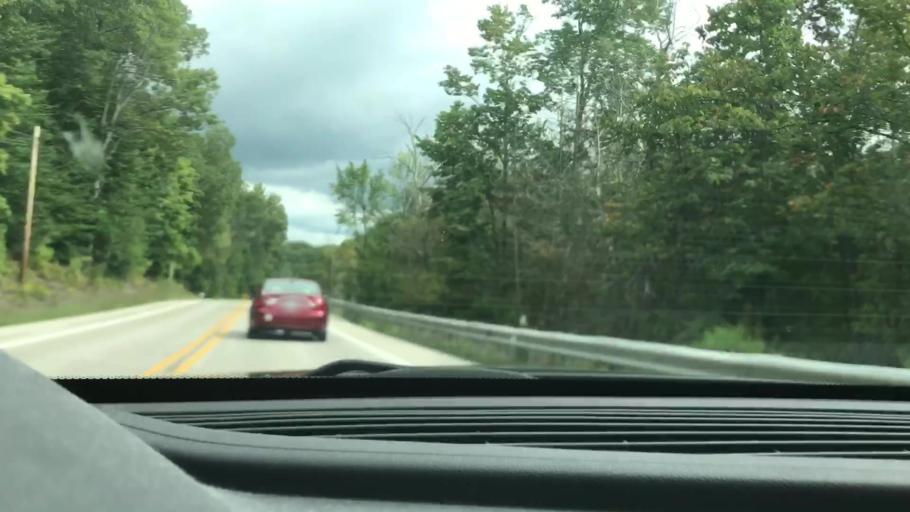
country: US
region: Michigan
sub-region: Antrim County
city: Bellaire
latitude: 45.0789
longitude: -85.2818
